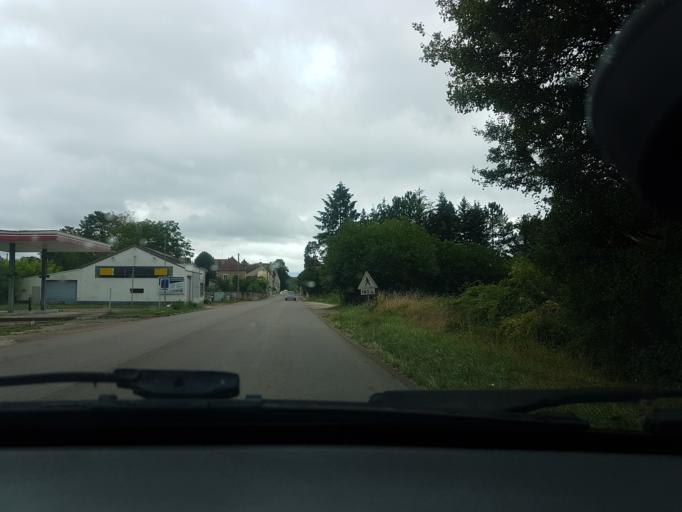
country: FR
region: Bourgogne
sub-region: Departement de l'Yonne
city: Vermenton
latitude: 47.6049
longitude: 3.7615
